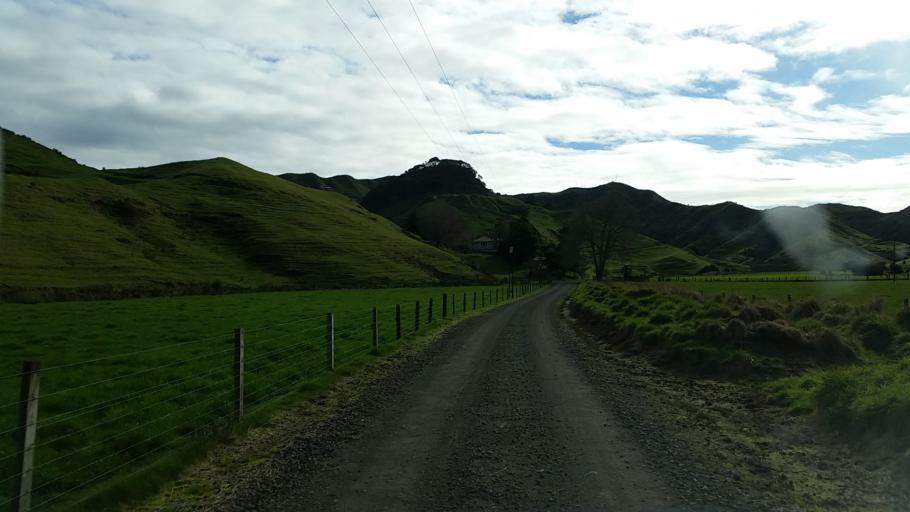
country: NZ
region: Taranaki
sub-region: South Taranaki District
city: Eltham
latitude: -39.2253
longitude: 174.5632
